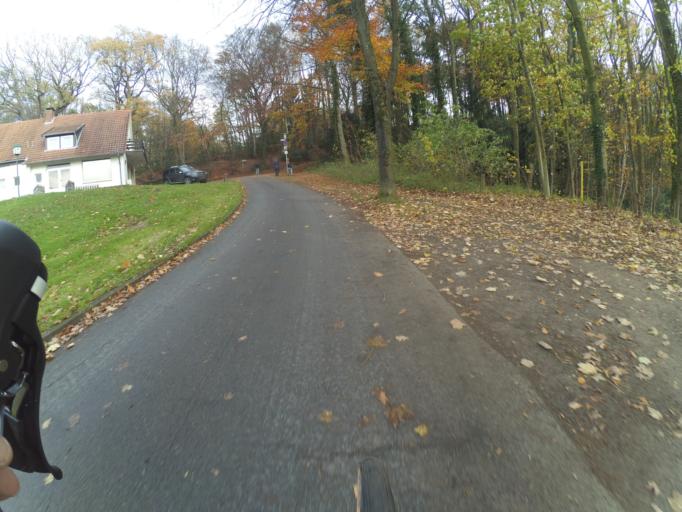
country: DE
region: North Rhine-Westphalia
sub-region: Regierungsbezirk Munster
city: Tecklenburg
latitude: 52.2245
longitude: 7.8105
